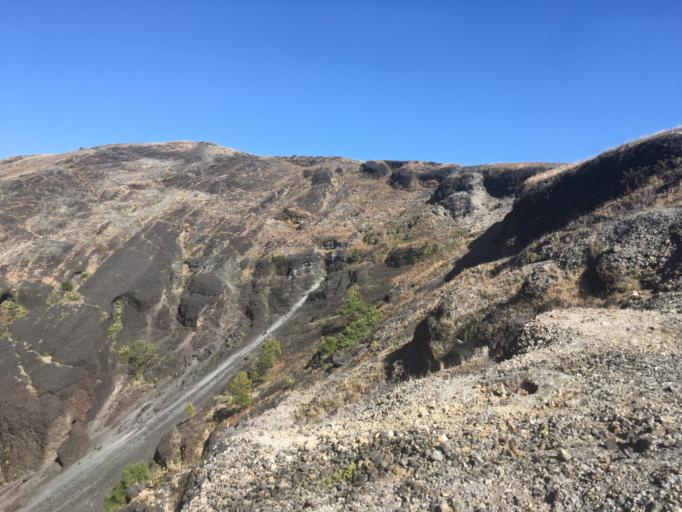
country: MX
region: Michoacan
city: Angahuan
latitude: 19.4926
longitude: -102.2522
